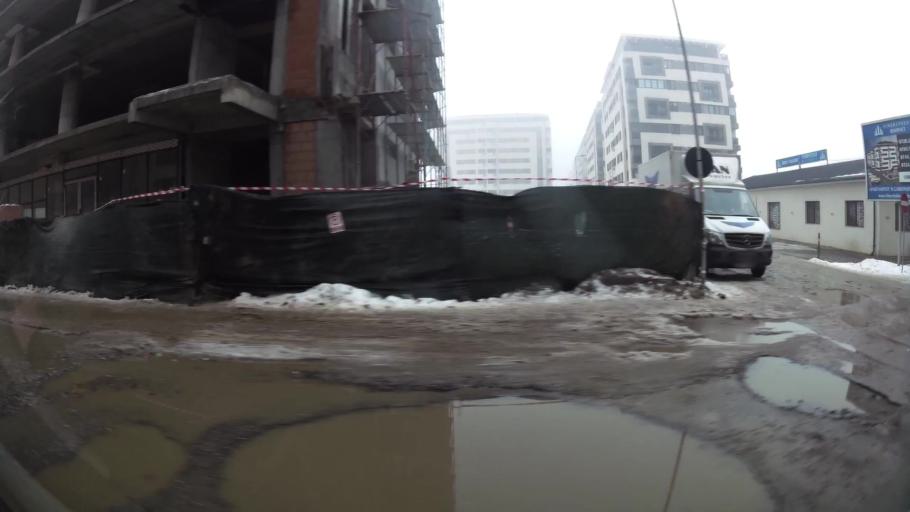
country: RO
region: Ilfov
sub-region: Comuna Chiajna
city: Chiajna
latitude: 44.4459
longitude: 25.9826
